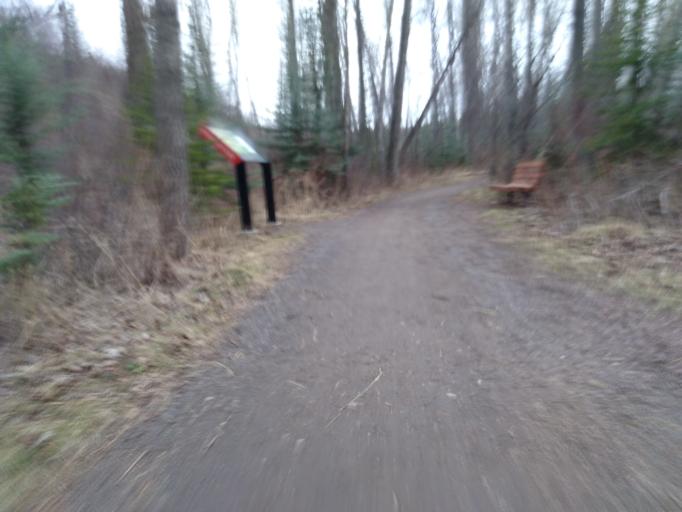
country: CA
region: Alberta
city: Cochrane
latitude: 51.1822
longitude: -114.4799
